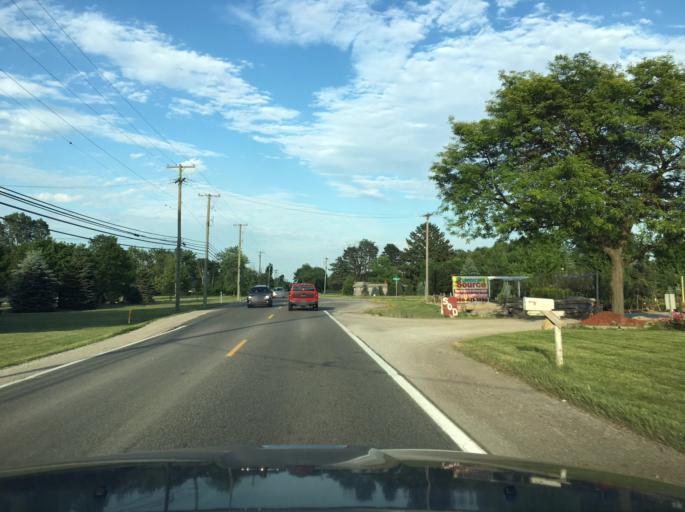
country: US
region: Michigan
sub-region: Macomb County
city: Shelby
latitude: 42.7163
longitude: -82.9518
